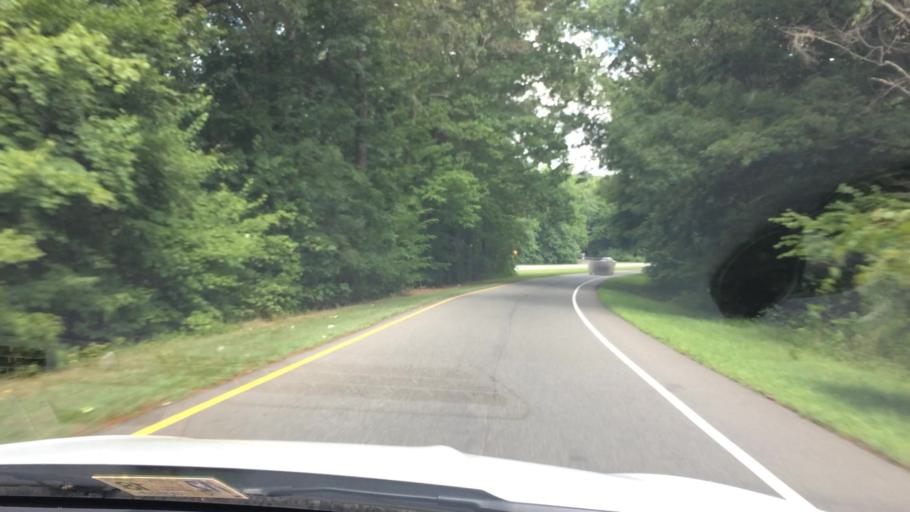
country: US
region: Virginia
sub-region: City of Poquoson
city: Poquoson
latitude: 37.1272
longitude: -76.4581
